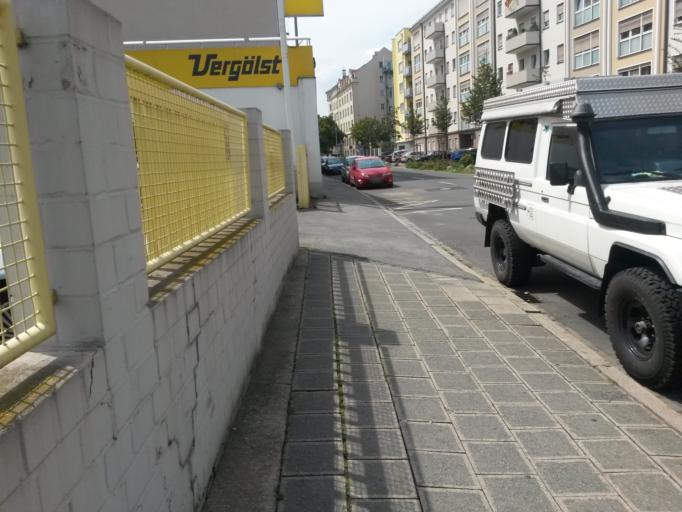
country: DE
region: Bavaria
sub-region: Regierungsbezirk Mittelfranken
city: Furth
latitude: 49.4674
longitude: 11.0113
